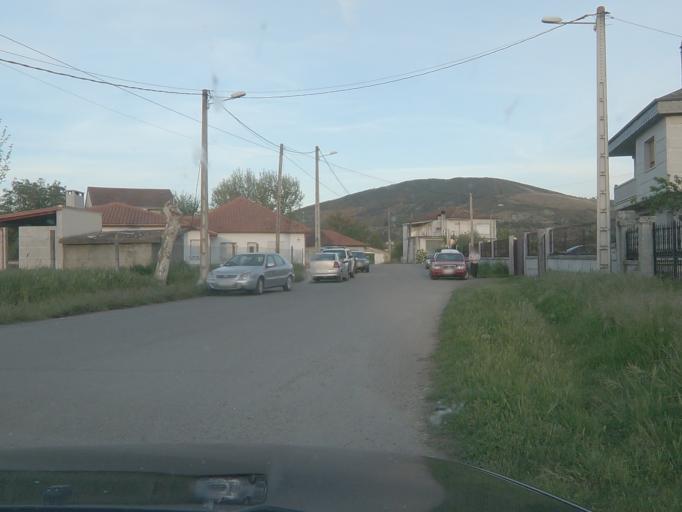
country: ES
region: Galicia
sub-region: Provincia de Ourense
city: Verin
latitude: 41.9183
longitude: -7.4446
